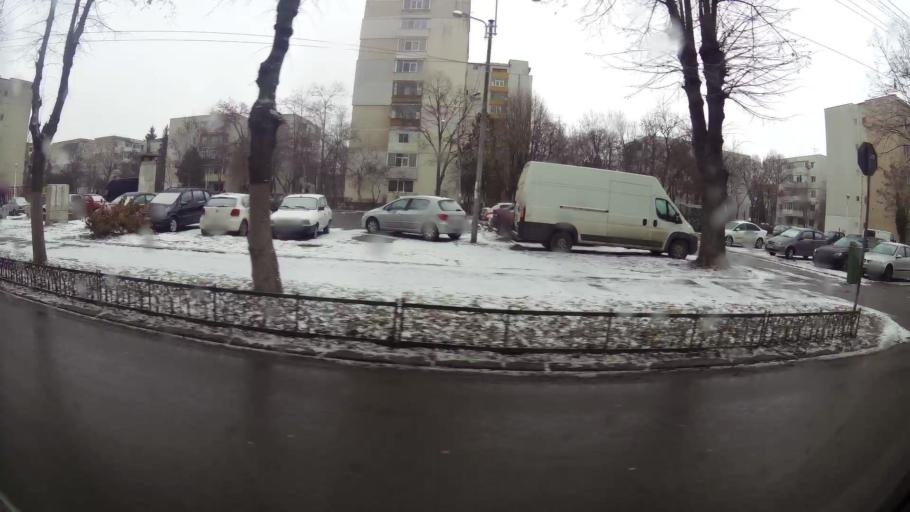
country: RO
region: Prahova
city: Ploiesti
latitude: 44.9563
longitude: 25.9973
